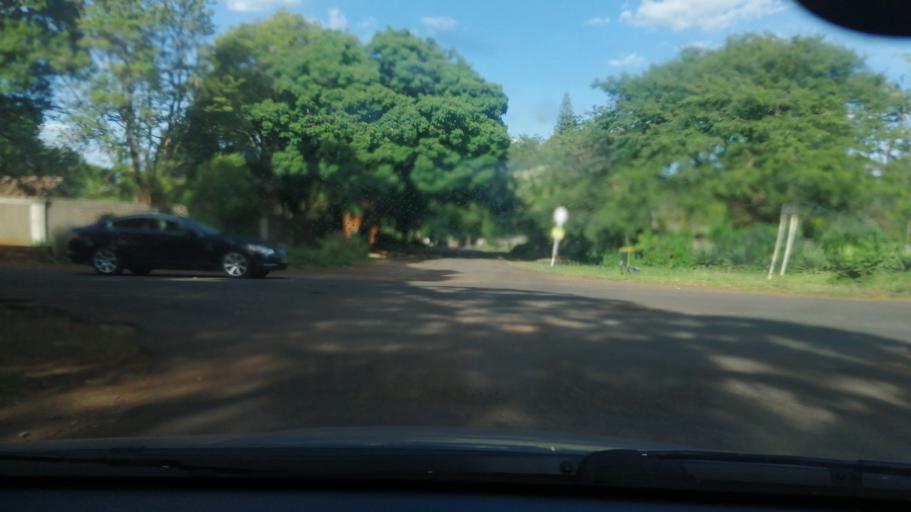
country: ZW
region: Harare
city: Harare
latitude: -17.7648
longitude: 31.0563
